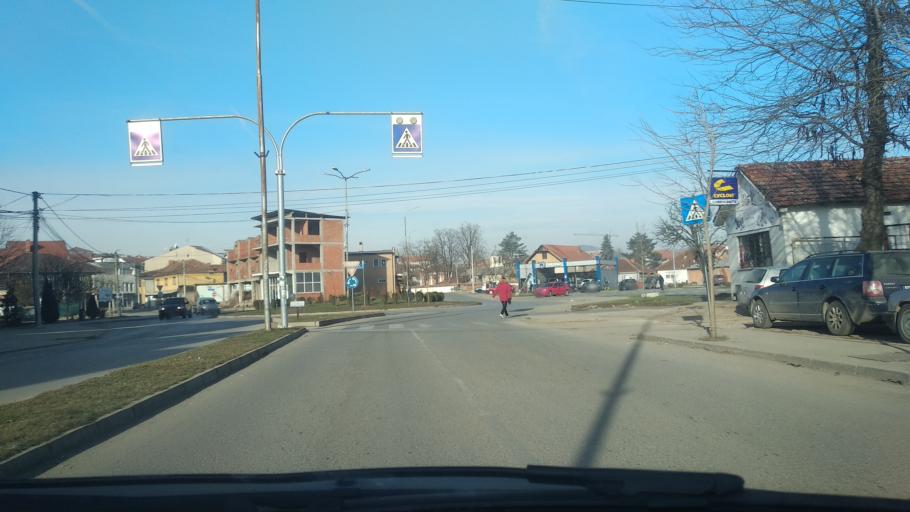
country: XK
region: Mitrovica
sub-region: Vushtrri
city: Vushtrri
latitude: 42.8199
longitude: 20.9770
